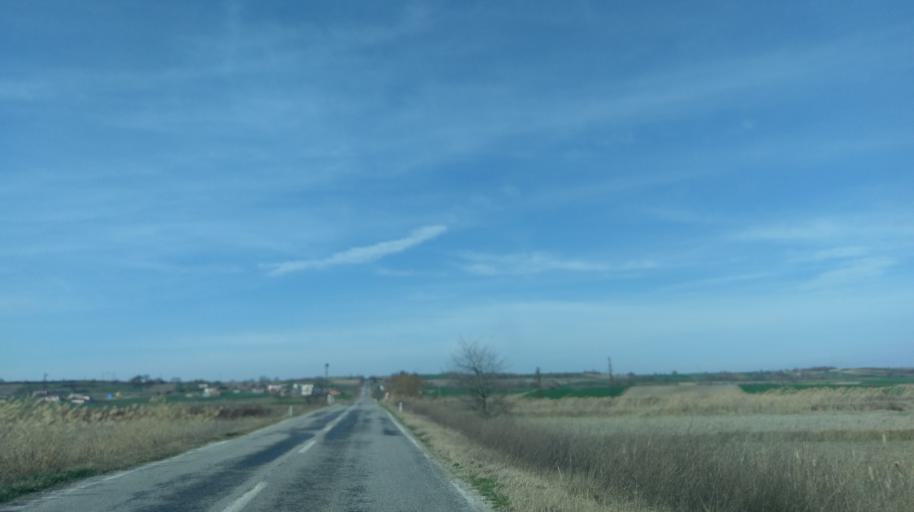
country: TR
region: Edirne
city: Copkoy
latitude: 41.2750
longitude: 26.8003
